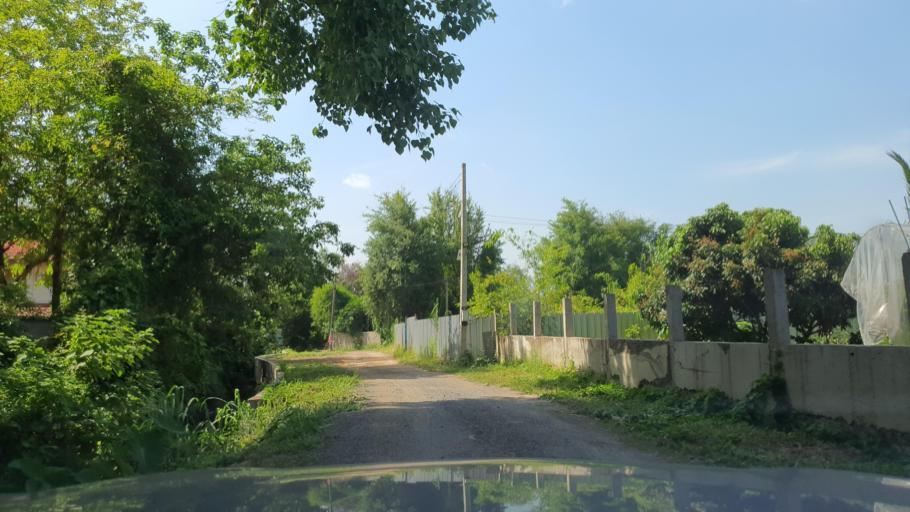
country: TH
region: Chiang Mai
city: Hang Dong
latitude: 18.7170
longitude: 98.9174
